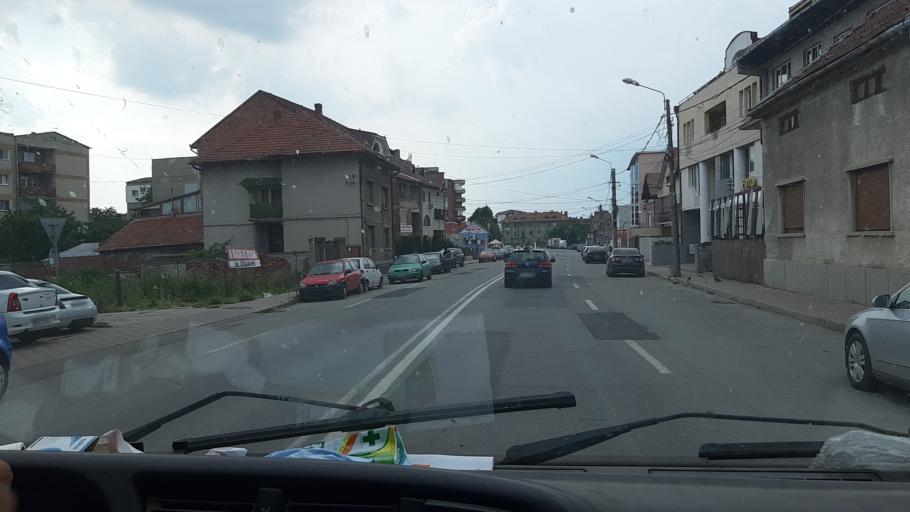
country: RO
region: Timis
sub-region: Municipiul Lugoj
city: Lugoj
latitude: 45.6957
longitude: 21.9006
